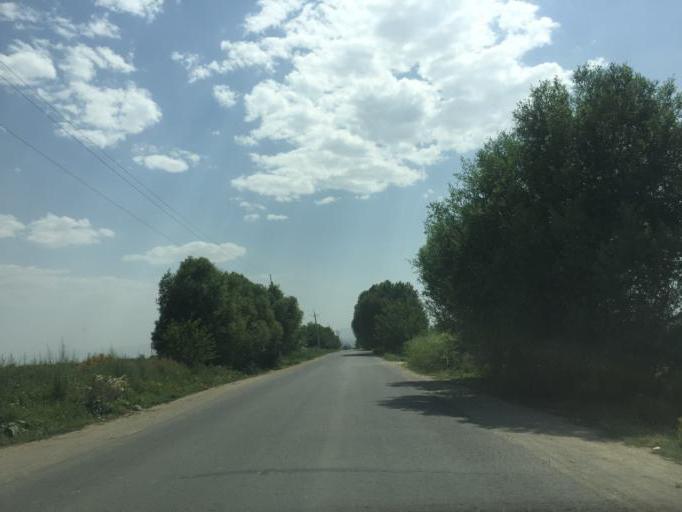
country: AM
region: Ararat
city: Shahumyan
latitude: 39.8930
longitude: 44.5955
